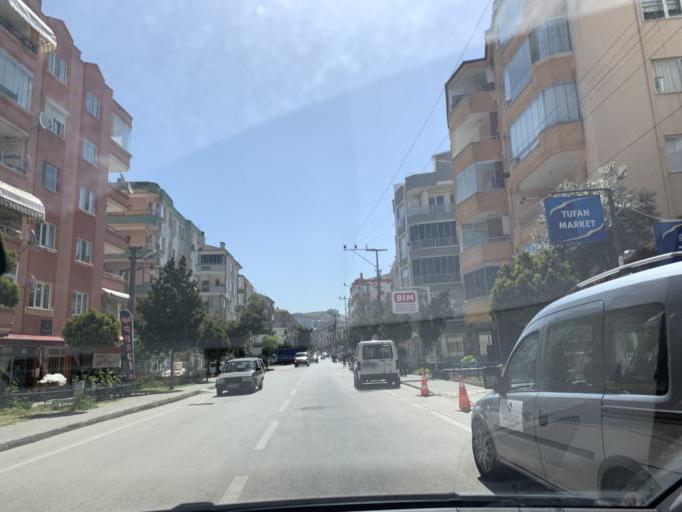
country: TR
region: Bursa
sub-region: Mudanya
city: Mudanya
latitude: 40.3560
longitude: 28.9216
